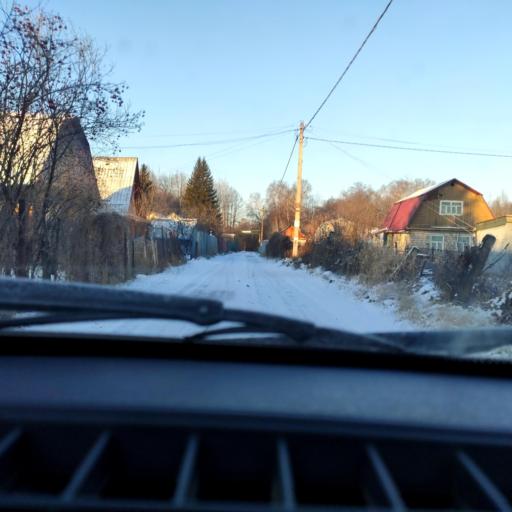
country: RU
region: Bashkortostan
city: Avdon
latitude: 54.6254
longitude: 55.7134
